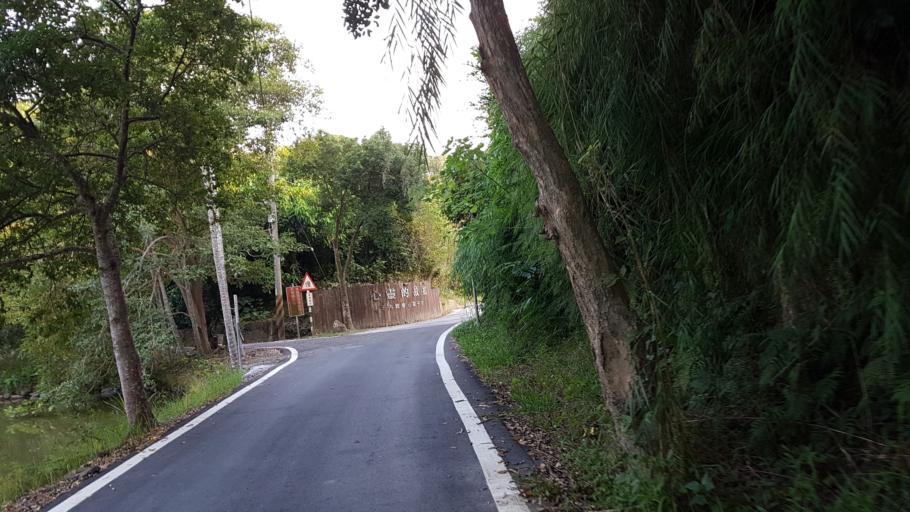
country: TW
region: Taiwan
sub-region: Chiayi
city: Jiayi Shi
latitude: 23.3621
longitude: 120.4678
